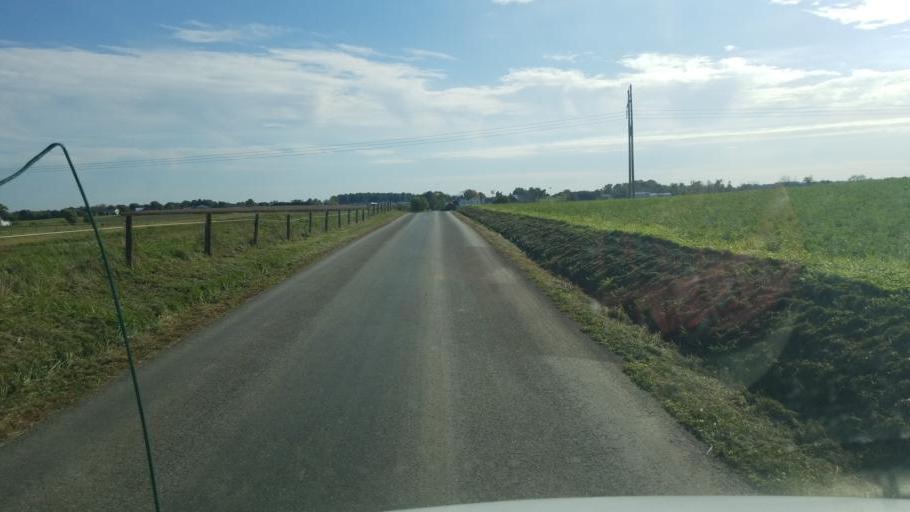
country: US
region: Ohio
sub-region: Wayne County
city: Apple Creek
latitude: 40.7375
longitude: -81.7878
